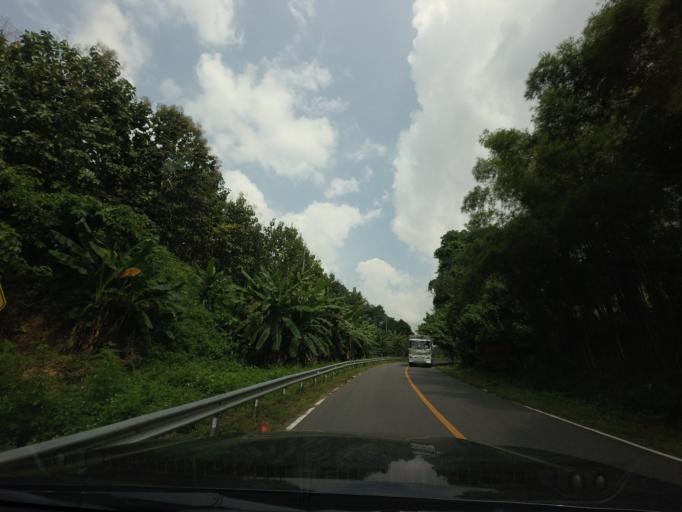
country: TH
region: Nan
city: Pua
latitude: 19.1803
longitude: 100.9598
